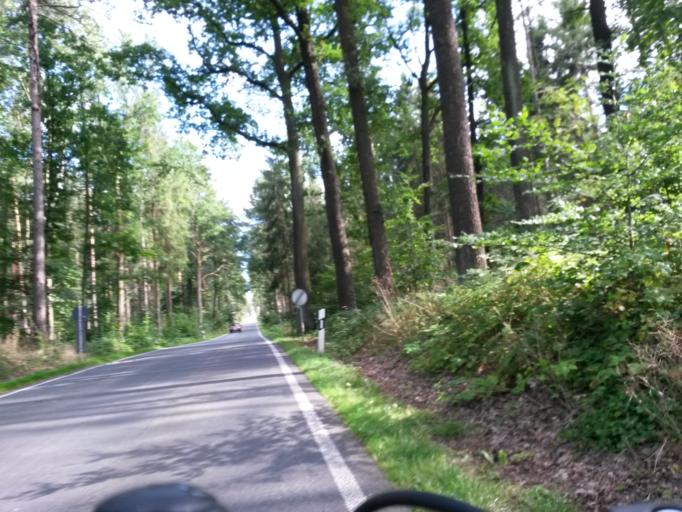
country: DE
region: Thuringia
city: Bad Klosterlausnitz
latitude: 50.9037
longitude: 11.8787
